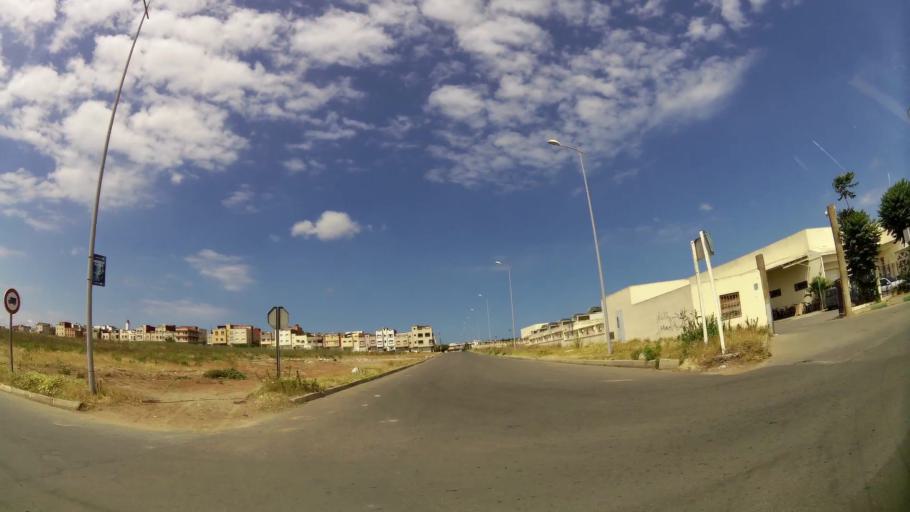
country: MA
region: Gharb-Chrarda-Beni Hssen
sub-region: Kenitra Province
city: Kenitra
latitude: 34.2467
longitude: -6.6078
